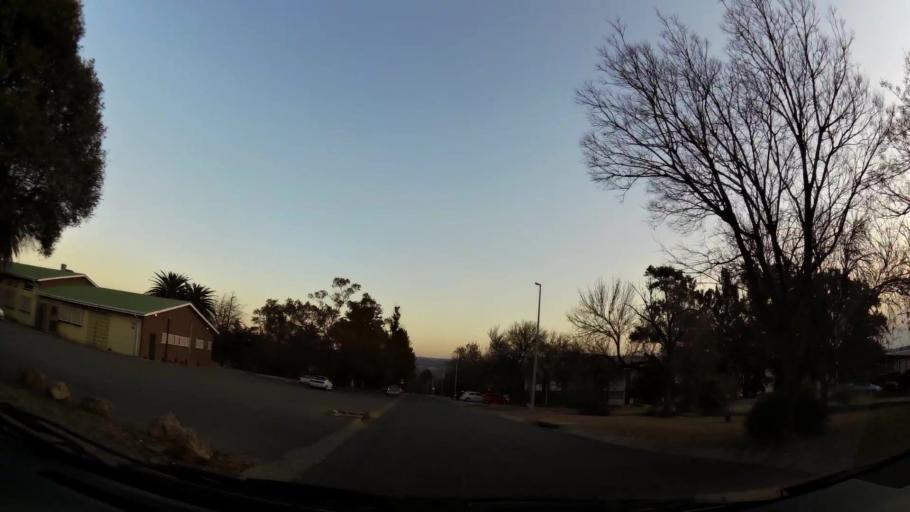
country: ZA
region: Gauteng
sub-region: City of Johannesburg Metropolitan Municipality
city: Diepsloot
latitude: -26.0027
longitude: 28.0453
